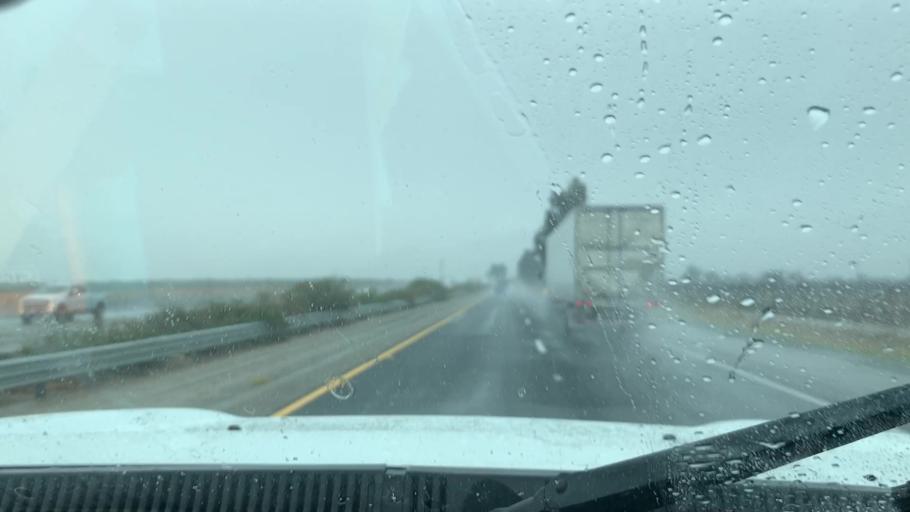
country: US
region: California
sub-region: Tulare County
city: Earlimart
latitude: 35.8632
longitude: -119.2692
